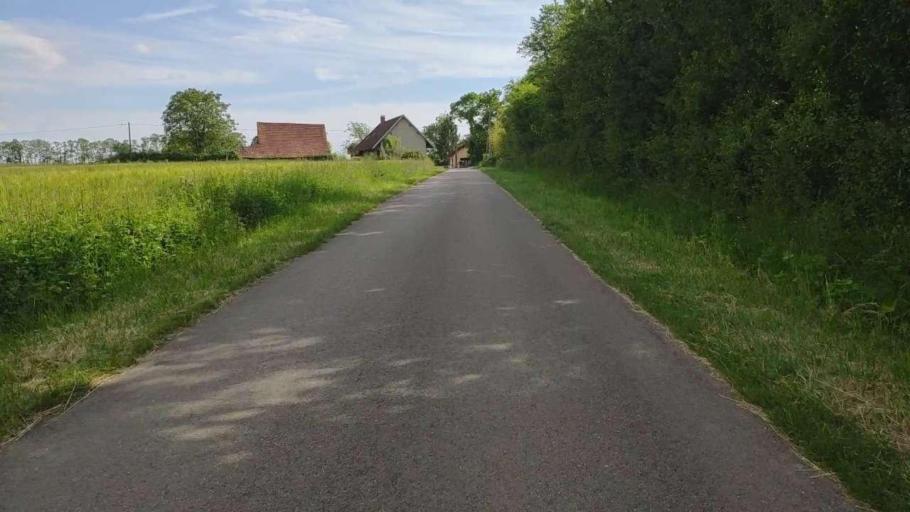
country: FR
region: Franche-Comte
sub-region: Departement du Jura
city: Bletterans
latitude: 46.8209
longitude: 5.3803
